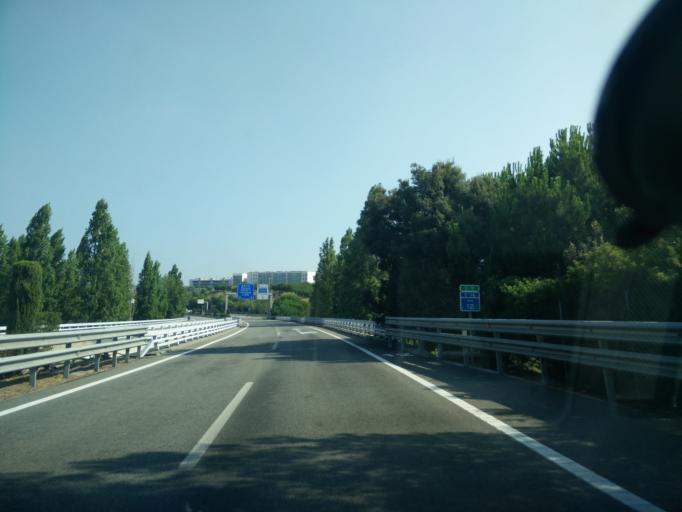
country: ES
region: Catalonia
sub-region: Provincia de Barcelona
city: Sant Cugat del Valles
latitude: 41.4782
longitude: 2.0658
